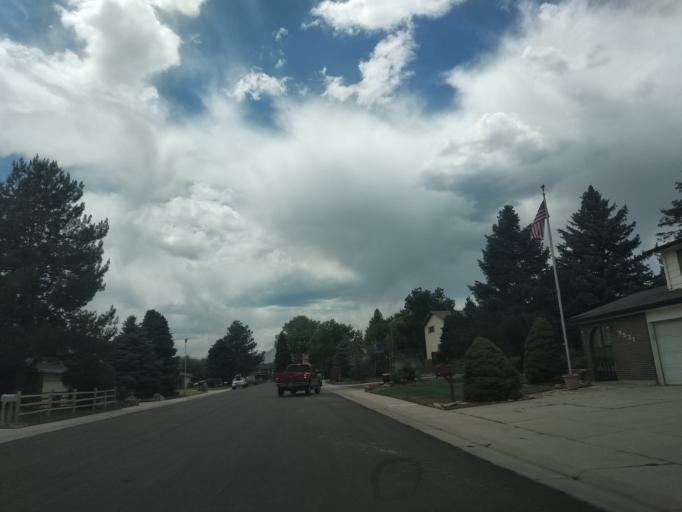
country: US
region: Colorado
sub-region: Jefferson County
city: Lakewood
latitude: 39.6717
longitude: -105.1028
